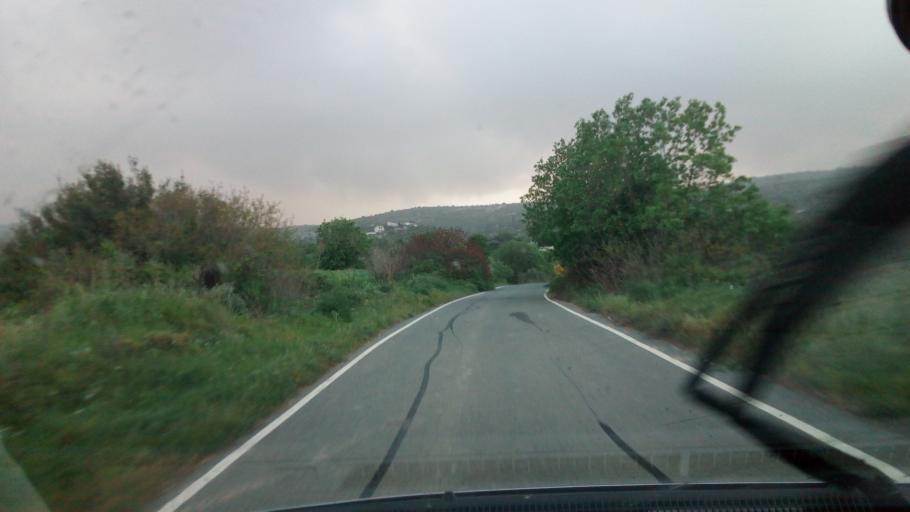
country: CY
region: Pafos
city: Polis
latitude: 34.9594
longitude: 32.4342
